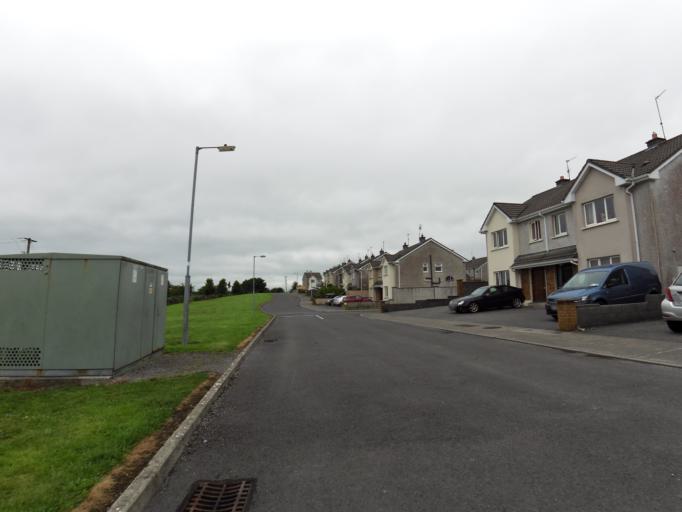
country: IE
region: Connaught
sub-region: County Galway
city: Loughrea
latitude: 53.2033
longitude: -8.5638
